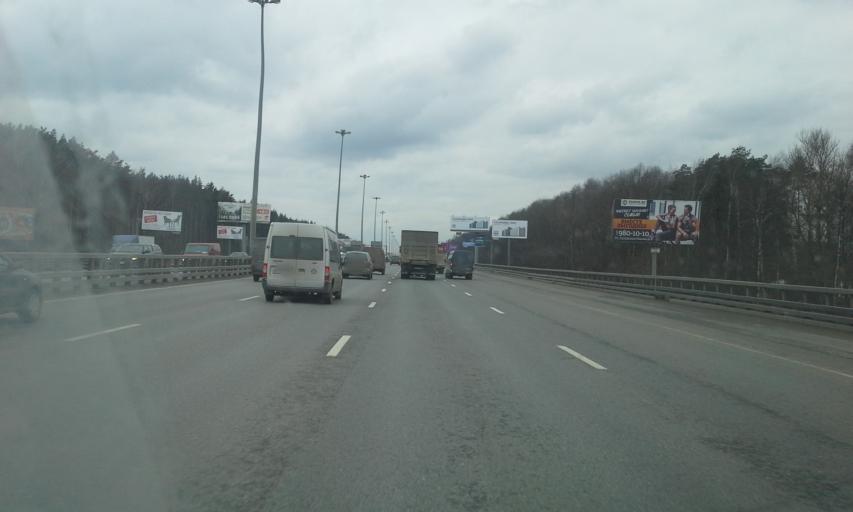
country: RU
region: Moscow
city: Solntsevo
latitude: 55.6263
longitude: 37.4195
